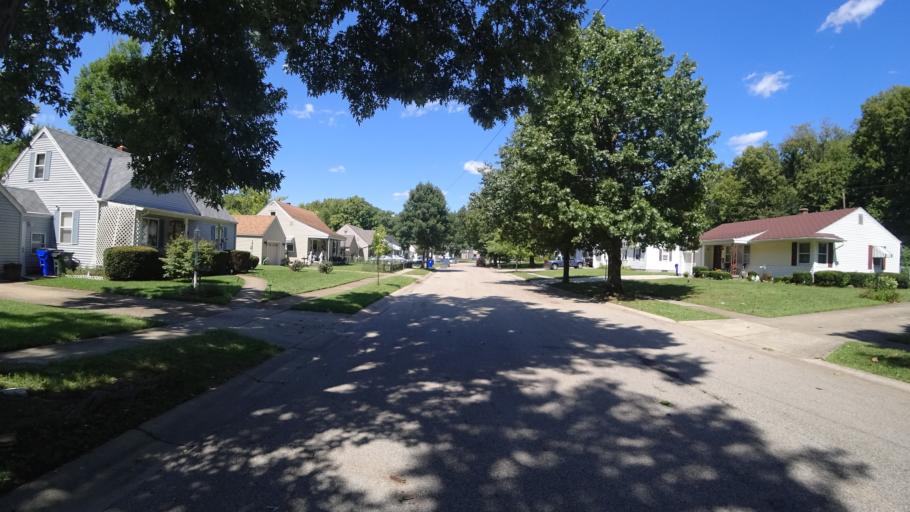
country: US
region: Ohio
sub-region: Butler County
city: New Miami
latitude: 39.4063
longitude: -84.5302
